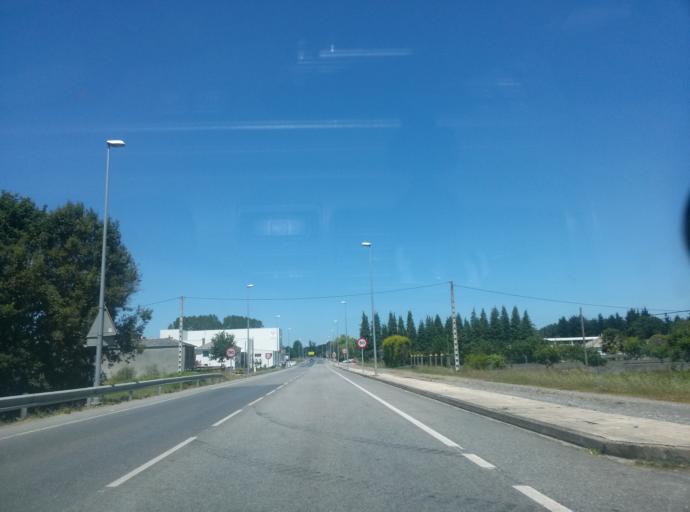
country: ES
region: Galicia
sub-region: Provincia de Lugo
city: Mos
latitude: 43.1325
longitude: -7.4890
